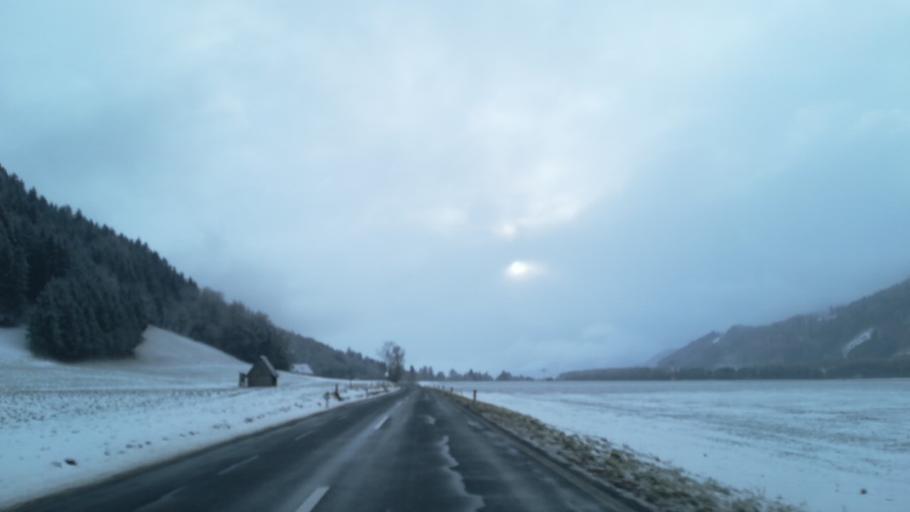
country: AT
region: Styria
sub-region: Politischer Bezirk Murtal
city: Poels
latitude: 47.2141
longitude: 14.6190
